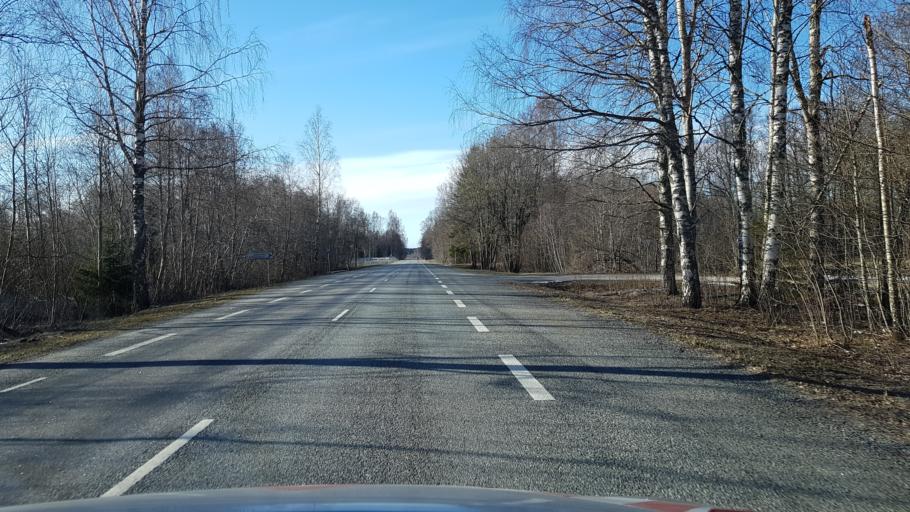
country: EE
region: Laeaene-Virumaa
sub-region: Tapa vald
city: Tapa
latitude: 59.4390
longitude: 25.9588
